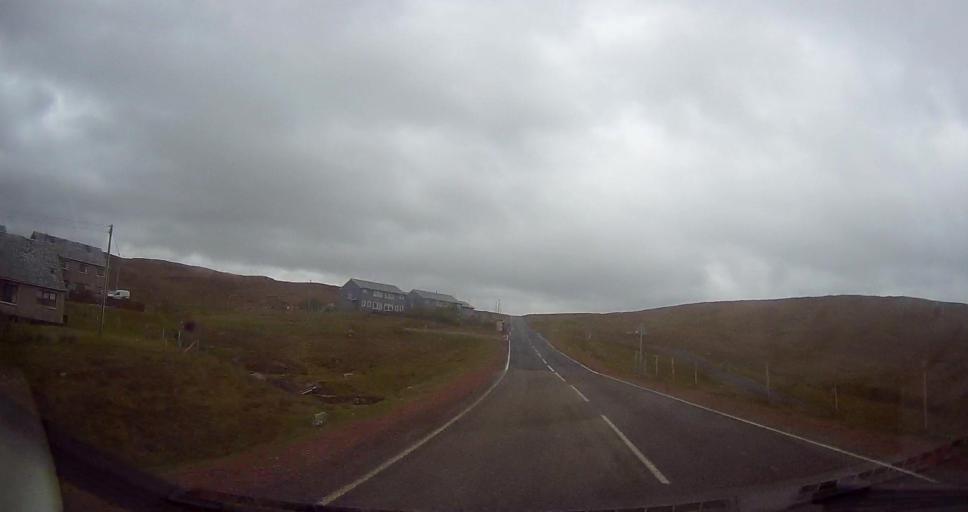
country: GB
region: Scotland
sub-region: Shetland Islands
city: Lerwick
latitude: 60.4883
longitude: -1.4507
